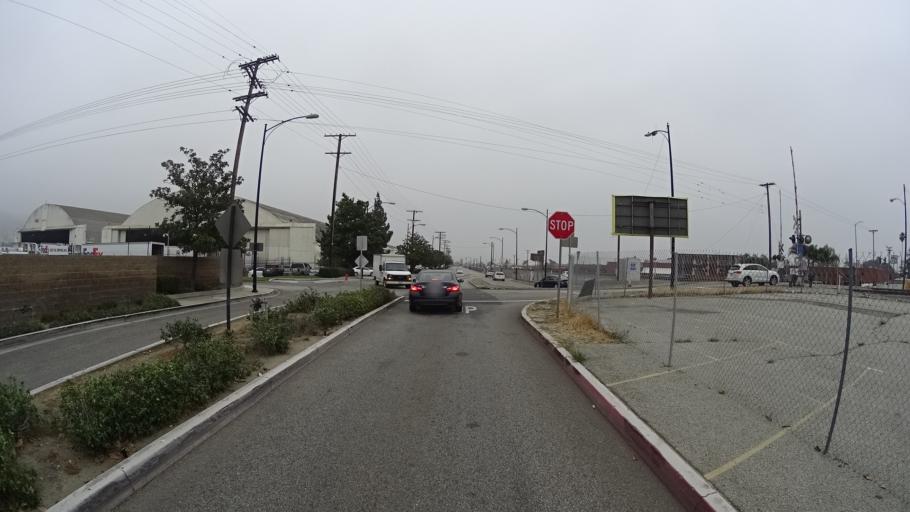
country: US
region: California
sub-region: Los Angeles County
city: North Hollywood
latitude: 34.1947
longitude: -118.3613
